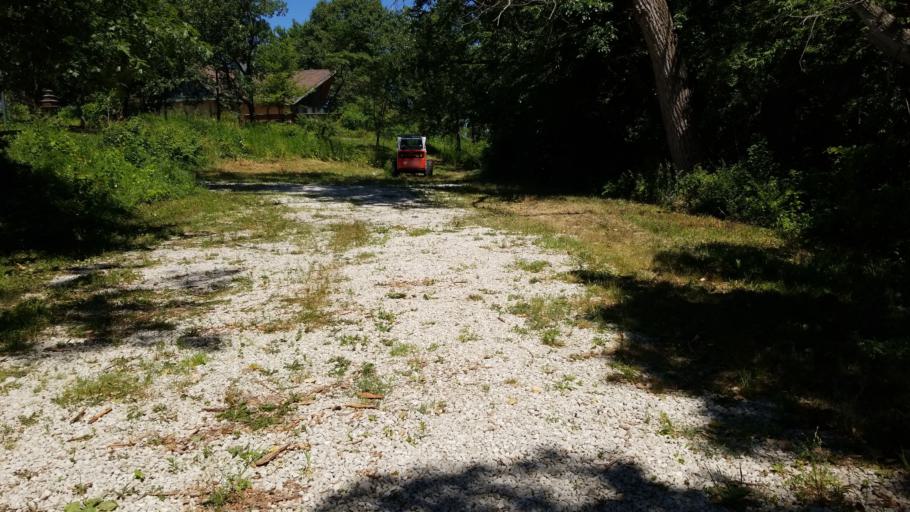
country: US
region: Iowa
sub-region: Pottawattamie County
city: Carter Lake
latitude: 41.3891
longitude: -95.9511
